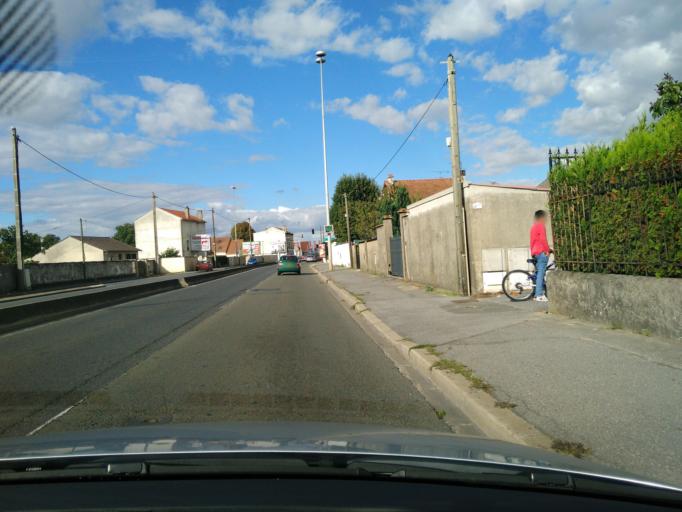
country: FR
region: Ile-de-France
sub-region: Departement de Seine-et-Marne
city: Meaux
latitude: 48.9447
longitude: 2.8795
